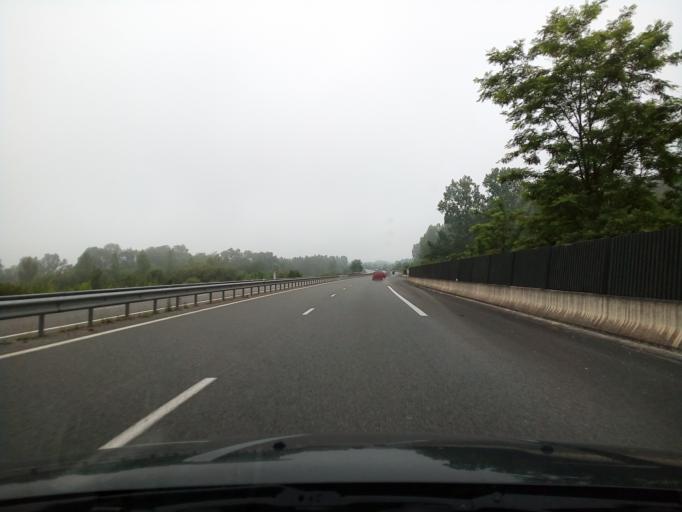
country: FR
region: Poitou-Charentes
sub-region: Departement de la Charente
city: Jarnac
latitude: 45.6759
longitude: -0.1547
